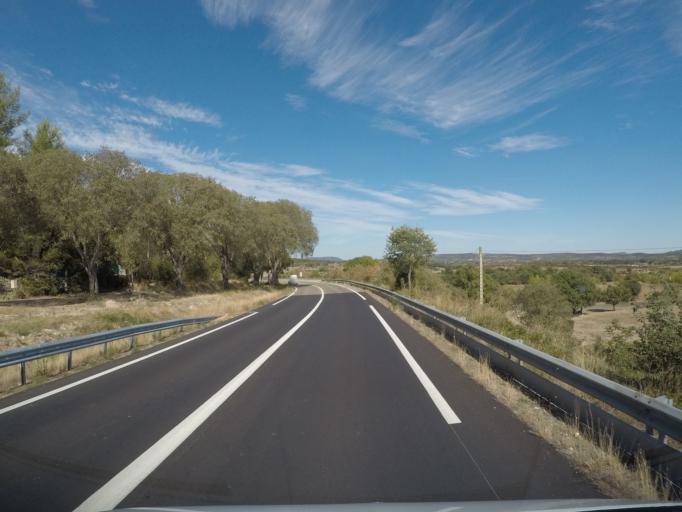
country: FR
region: Languedoc-Roussillon
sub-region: Departement de l'Herault
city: Saint-Martin-de-Londres
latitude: 43.8078
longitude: 3.7410
